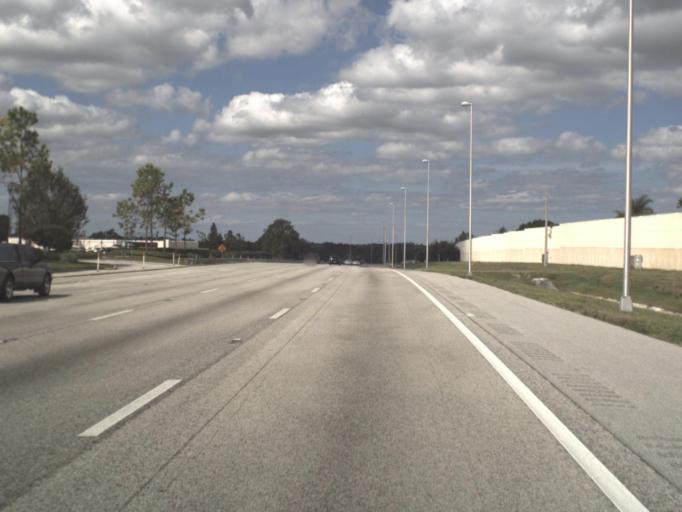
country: US
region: Florida
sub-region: Orange County
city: Gotha
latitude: 28.5176
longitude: -81.5018
